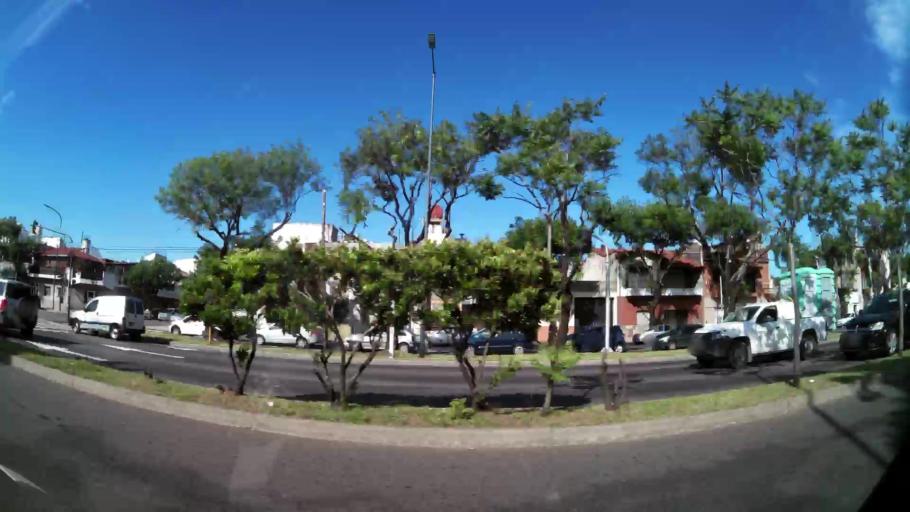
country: AR
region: Buenos Aires
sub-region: Partido de General San Martin
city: General San Martin
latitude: -34.5501
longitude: -58.4918
